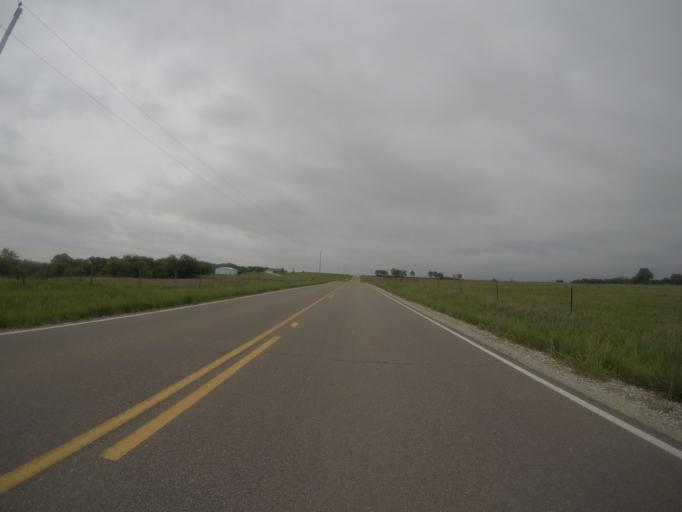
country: US
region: Kansas
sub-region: Pottawatomie County
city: Westmoreland
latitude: 39.5115
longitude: -96.2108
